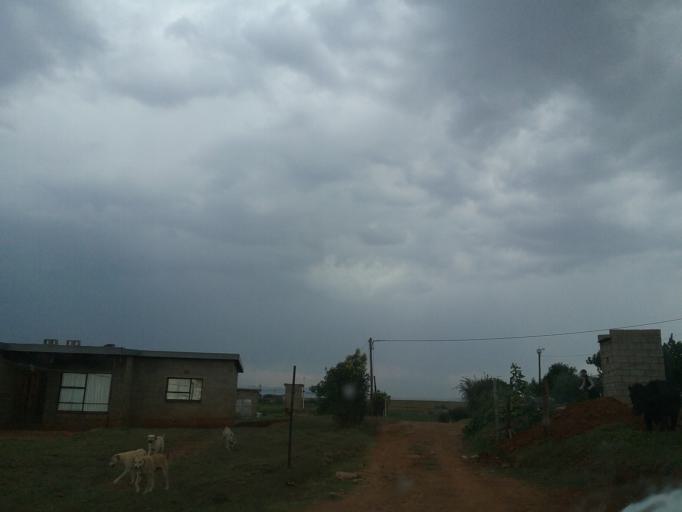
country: LS
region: Maseru
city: Maseru
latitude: -29.4211
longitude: 27.5688
